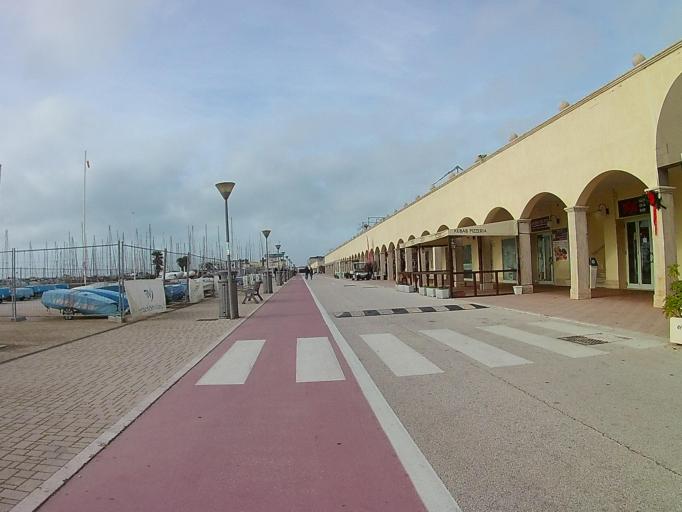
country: IT
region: Latium
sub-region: Citta metropolitana di Roma Capitale
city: Lido di Ostia
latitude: 41.7386
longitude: 12.2469
